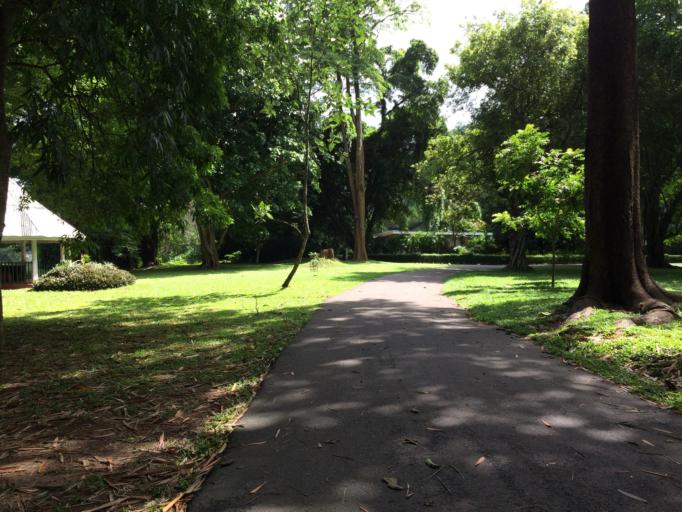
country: LK
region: Central
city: Kandy
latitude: 7.2754
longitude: 80.5927
